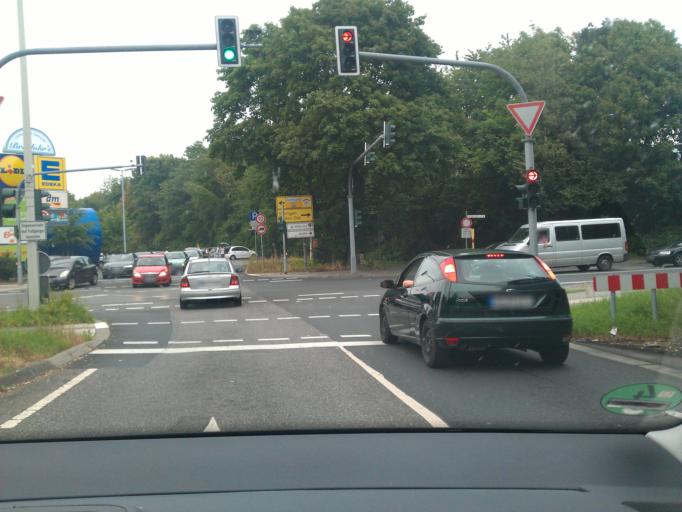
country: DE
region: North Rhine-Westphalia
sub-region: Regierungsbezirk Dusseldorf
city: Hilden
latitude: 51.1678
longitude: 6.9536
